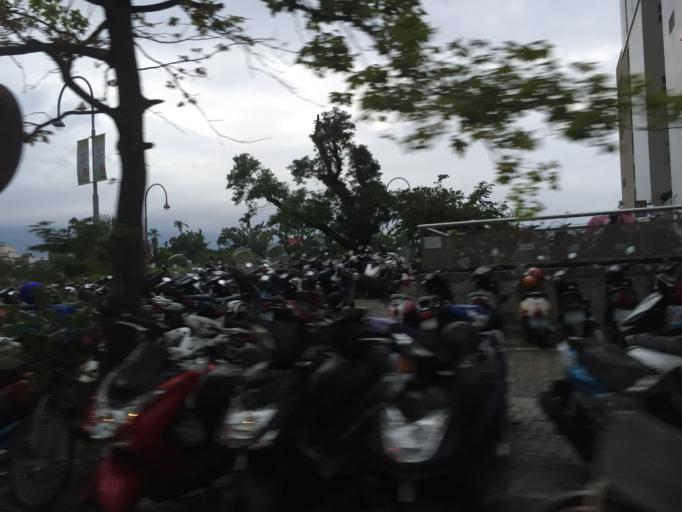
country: TW
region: Taiwan
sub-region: Yilan
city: Yilan
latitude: 24.7537
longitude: 121.7499
